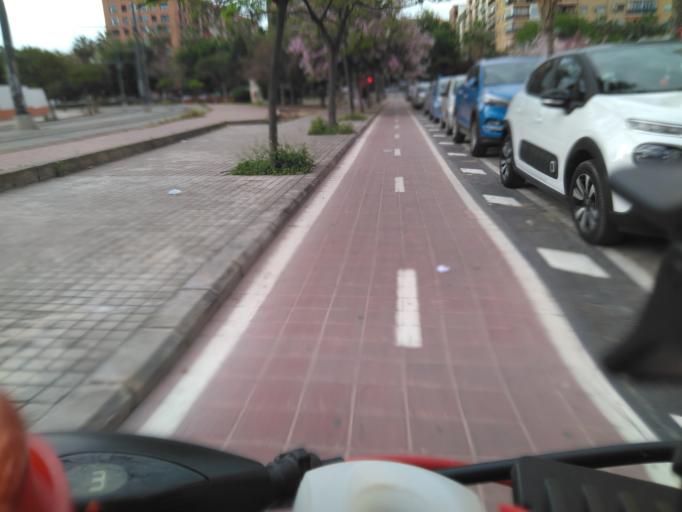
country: ES
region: Valencia
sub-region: Provincia de Valencia
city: Valencia
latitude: 39.4867
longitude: -0.3836
